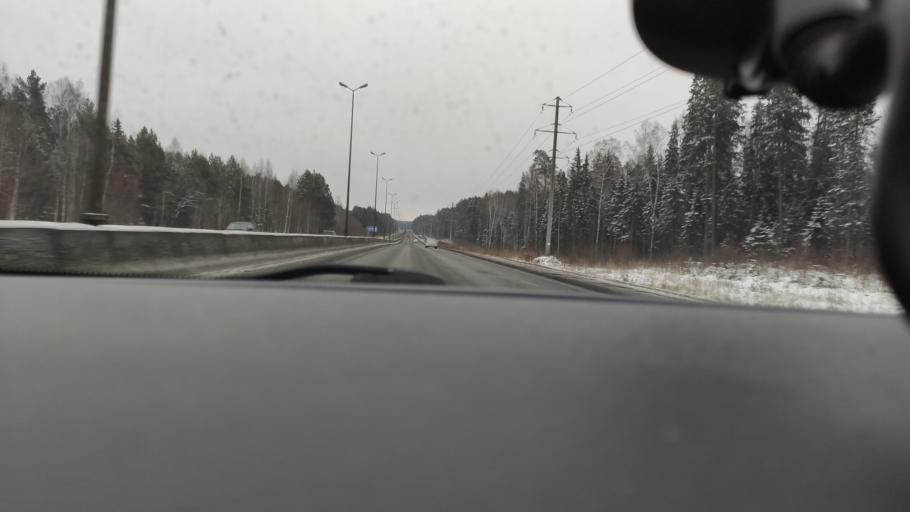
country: RU
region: Perm
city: Kondratovo
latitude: 58.0527
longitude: 56.1441
